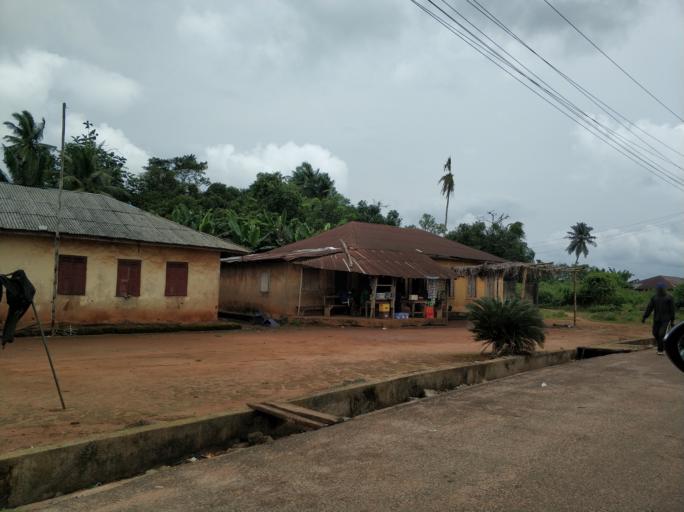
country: NG
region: Ogun
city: Abigi
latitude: 6.6132
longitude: 4.5444
